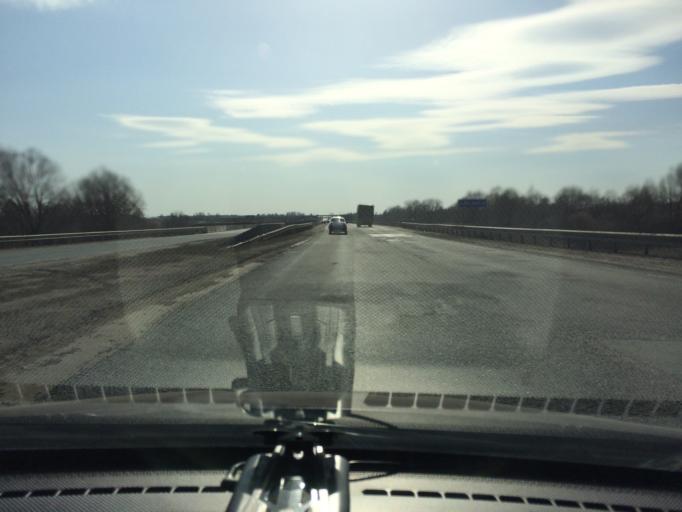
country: RU
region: Mariy-El
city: Yoshkar-Ola
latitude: 56.6876
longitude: 48.0432
